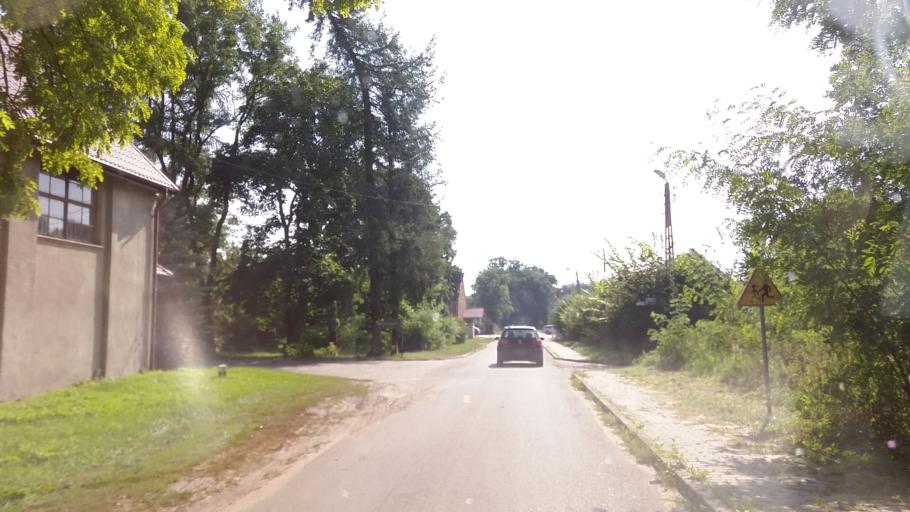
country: PL
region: Greater Poland Voivodeship
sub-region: Powiat czarnkowsko-trzcianecki
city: Krzyz Wielkopolski
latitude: 53.0479
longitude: 15.9433
